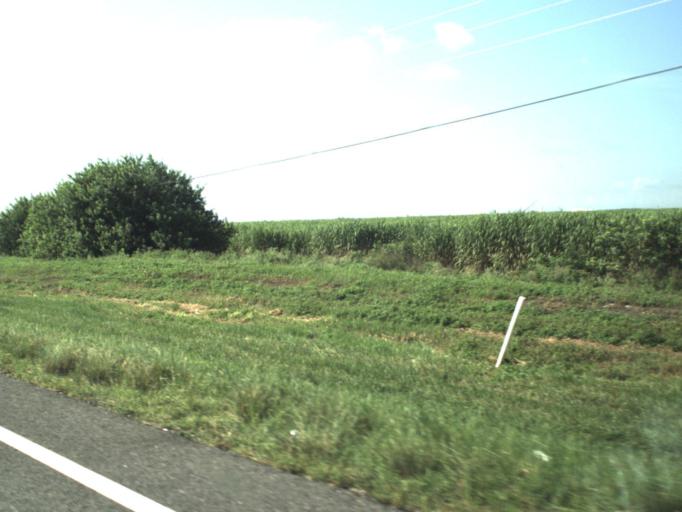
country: US
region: Florida
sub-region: Palm Beach County
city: Belle Glade Camp
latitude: 26.5166
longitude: -80.6789
